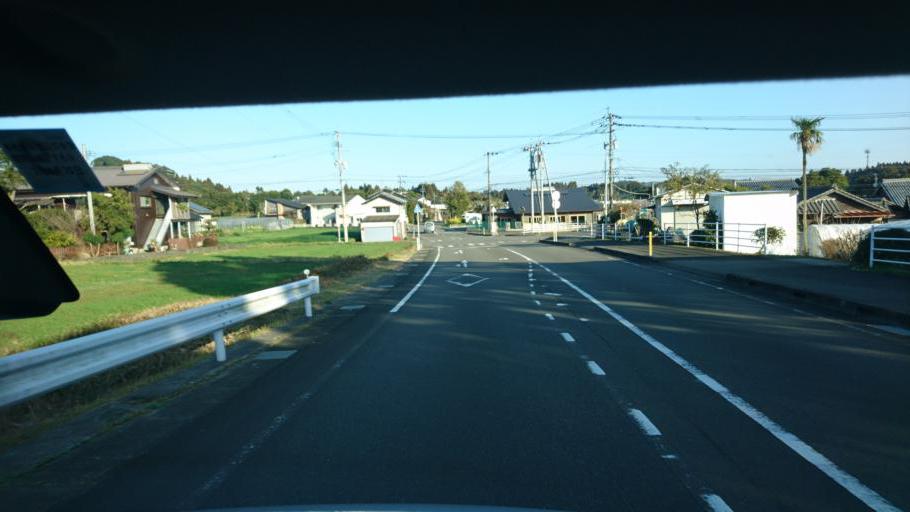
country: JP
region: Miyazaki
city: Miyazaki-shi
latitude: 31.8531
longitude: 131.3747
